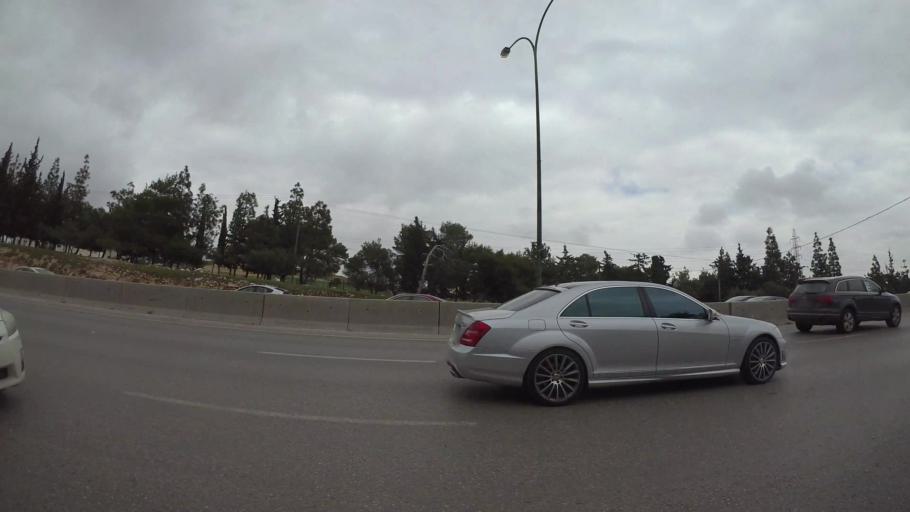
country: JO
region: Amman
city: Umm as Summaq
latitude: 31.9276
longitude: 35.8601
